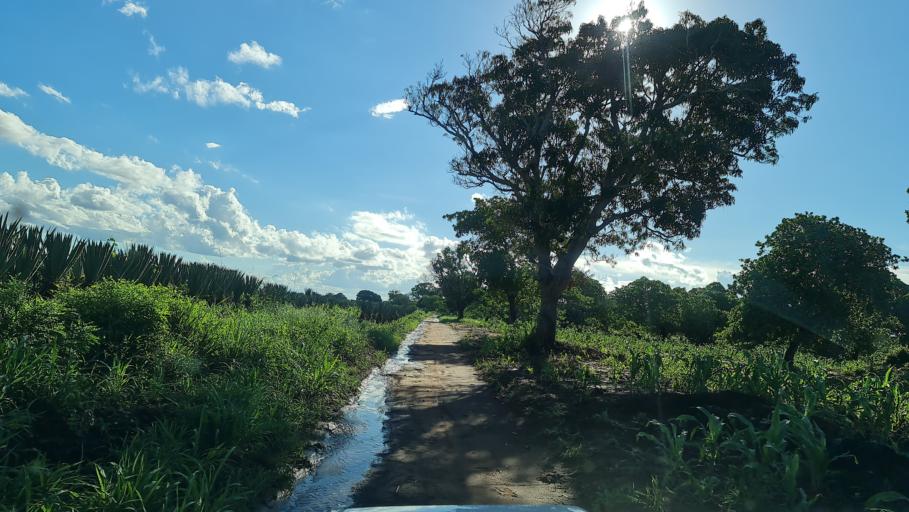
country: MZ
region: Nampula
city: Ilha de Mocambique
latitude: -14.9354
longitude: 40.2076
